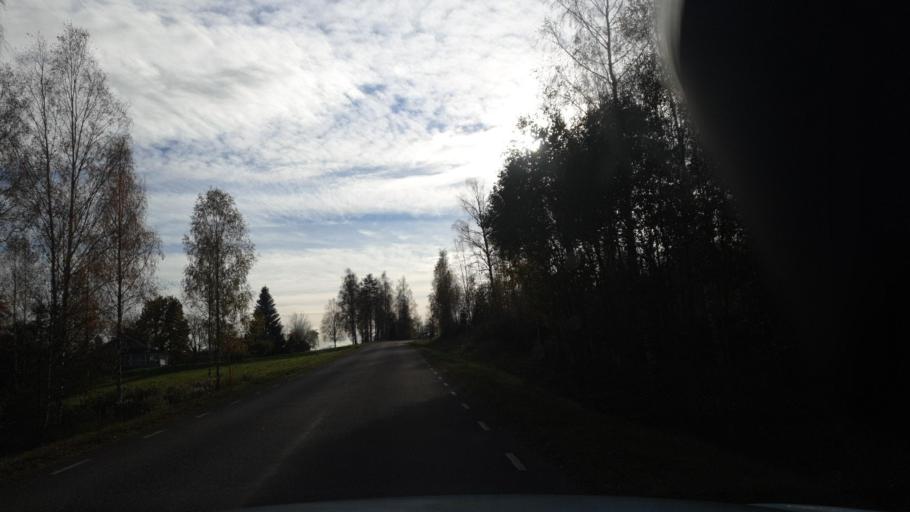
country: SE
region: Vaermland
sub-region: Eda Kommun
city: Charlottenberg
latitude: 59.9598
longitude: 12.3962
